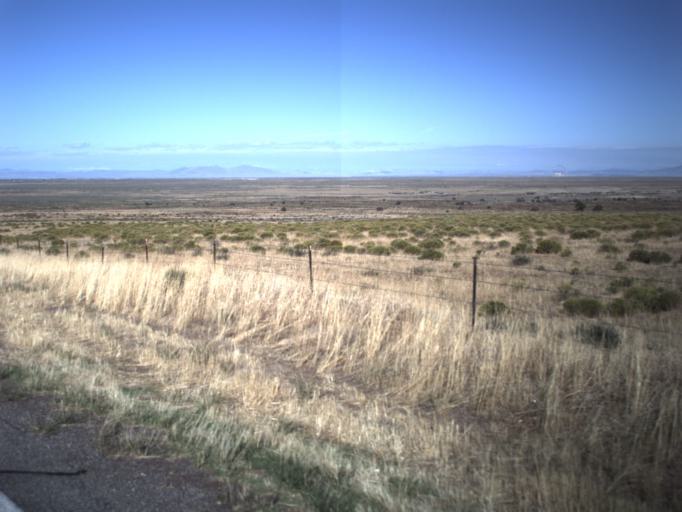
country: US
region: Utah
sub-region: Millard County
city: Delta
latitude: 39.3551
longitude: -112.3645
